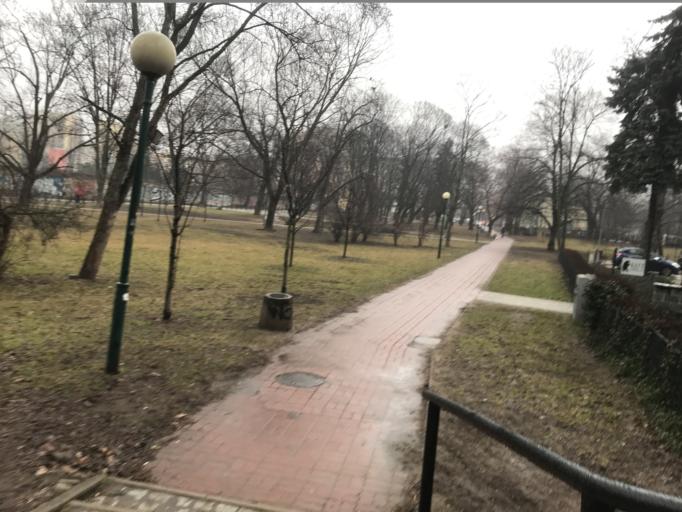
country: PL
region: Masovian Voivodeship
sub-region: Warszawa
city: Srodmiescie
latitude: 52.2341
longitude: 21.0270
